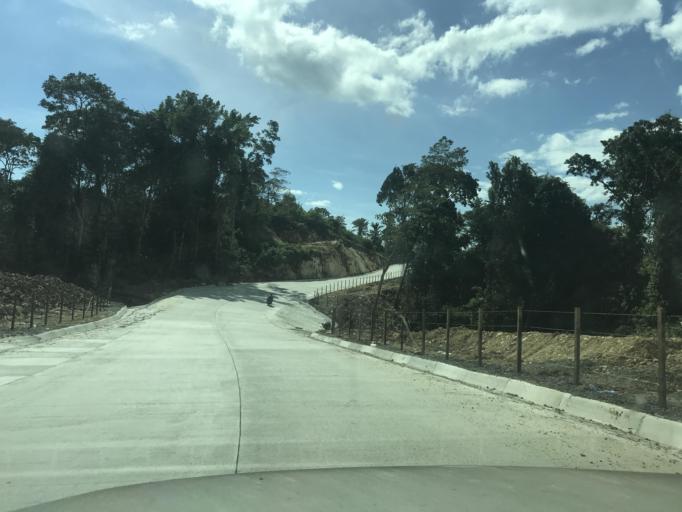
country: GT
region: Izabal
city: Morales
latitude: 15.6421
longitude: -89.0324
